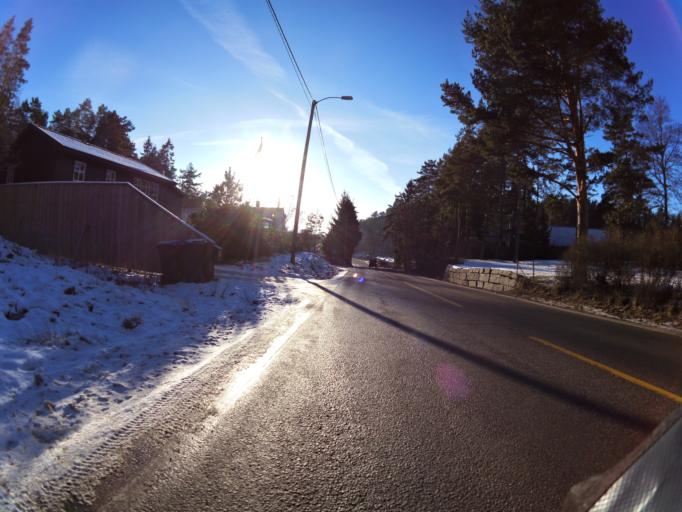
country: NO
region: Ostfold
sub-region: Fredrikstad
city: Lervik
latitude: 59.2255
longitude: 10.8015
